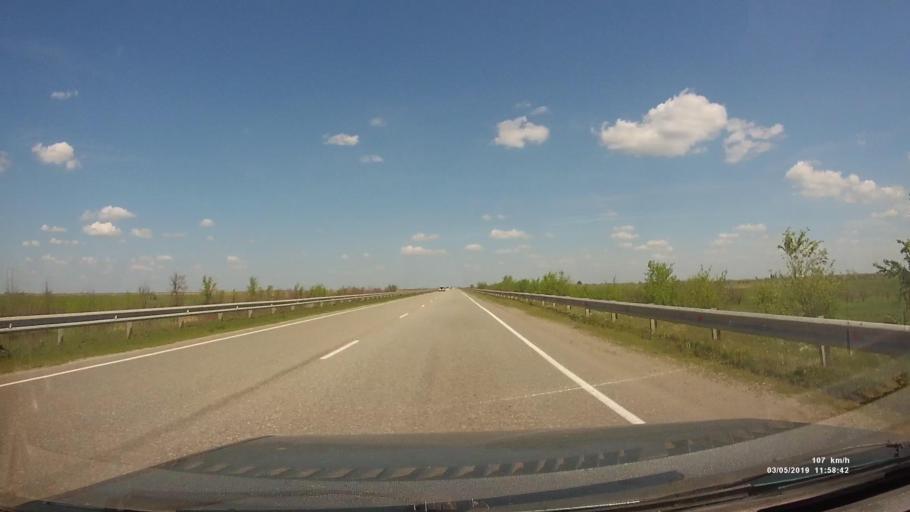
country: RU
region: Rostov
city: Bagayevskaya
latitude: 47.2246
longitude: 40.3228
